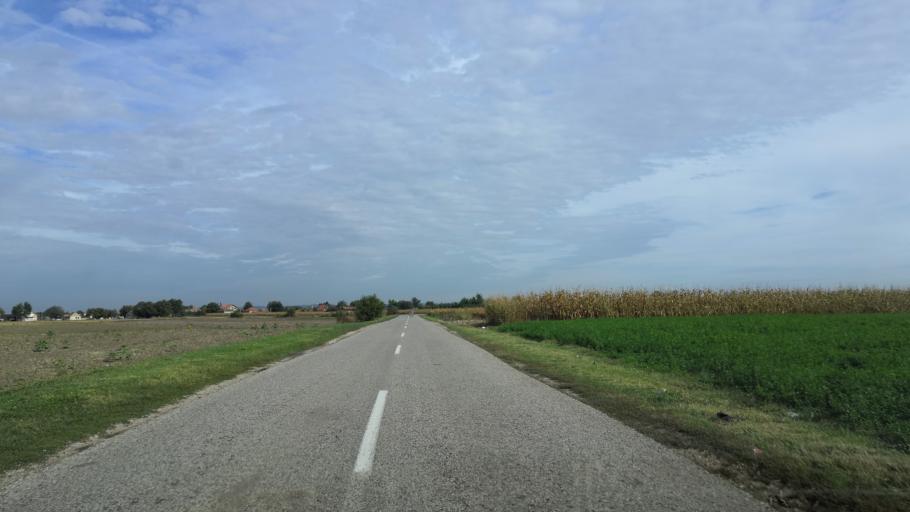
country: RS
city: Novi Karlovci
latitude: 45.0613
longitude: 20.1797
